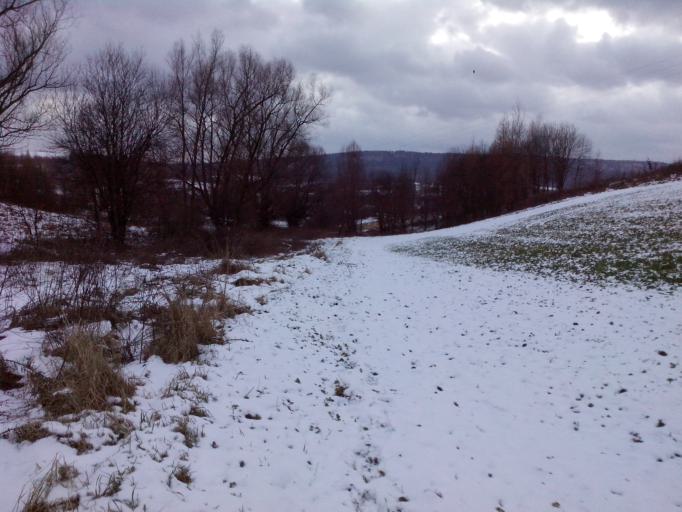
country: PL
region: Subcarpathian Voivodeship
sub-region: Powiat strzyzowski
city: Jawornik
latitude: 49.8395
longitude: 21.8408
